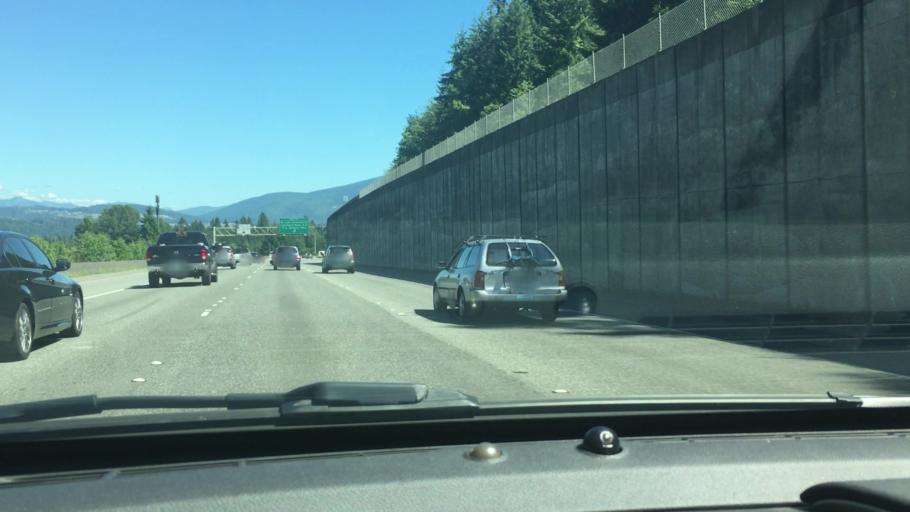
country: US
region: Washington
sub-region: King County
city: West Lake Sammamish
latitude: 47.5695
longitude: -122.1086
